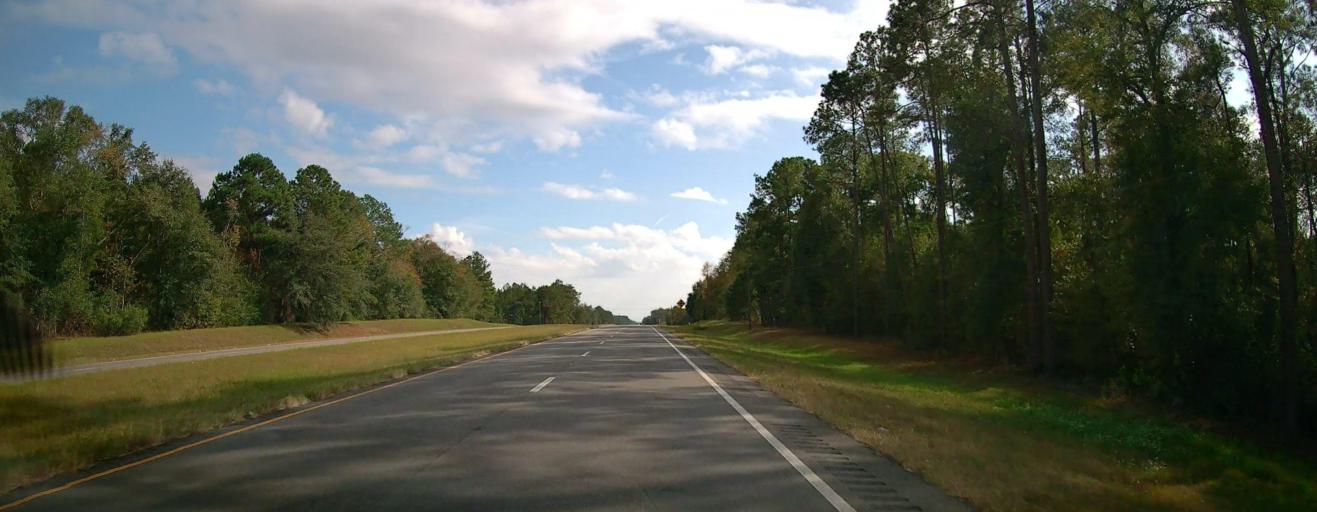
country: US
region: Georgia
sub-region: Thomas County
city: Meigs
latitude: 30.9971
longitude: -84.0466
